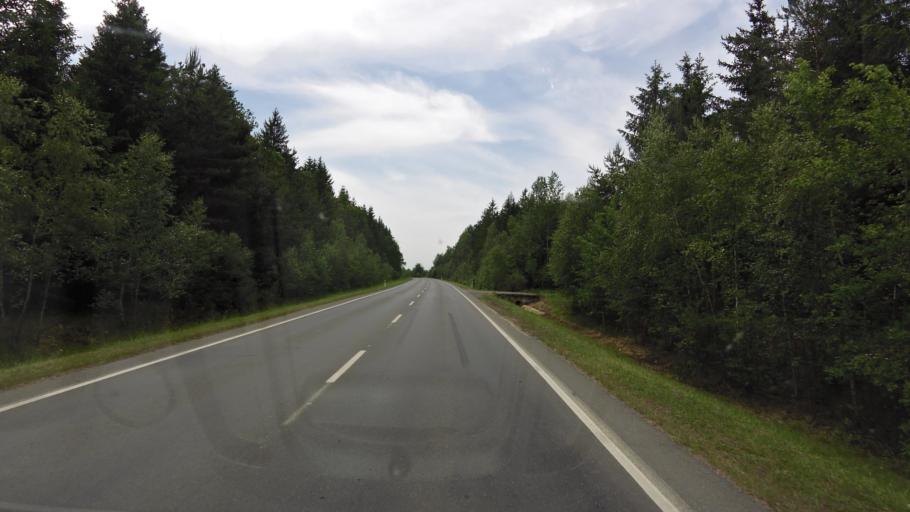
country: CZ
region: Plzensky
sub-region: Okres Rokycany
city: Rokycany
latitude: 49.7178
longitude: 13.5609
